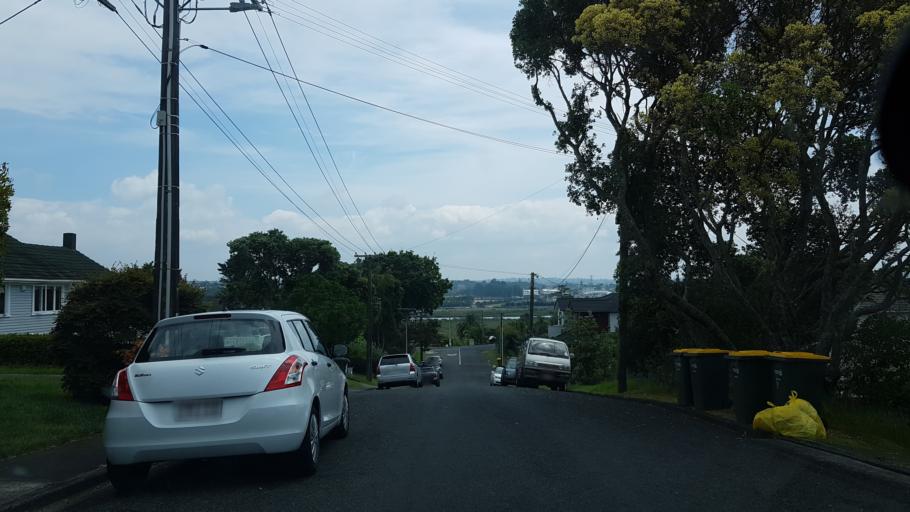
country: NZ
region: Auckland
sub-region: Auckland
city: North Shore
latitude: -36.8009
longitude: 174.7723
